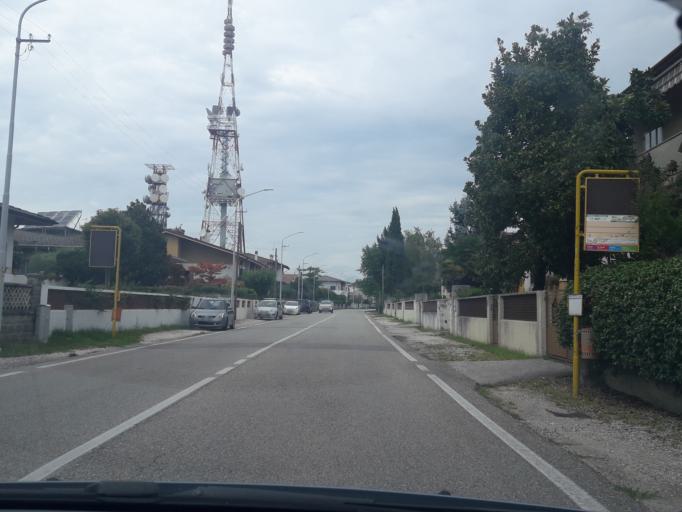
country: IT
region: Friuli Venezia Giulia
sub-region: Provincia di Udine
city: Udine
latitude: 46.0362
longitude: 13.2566
